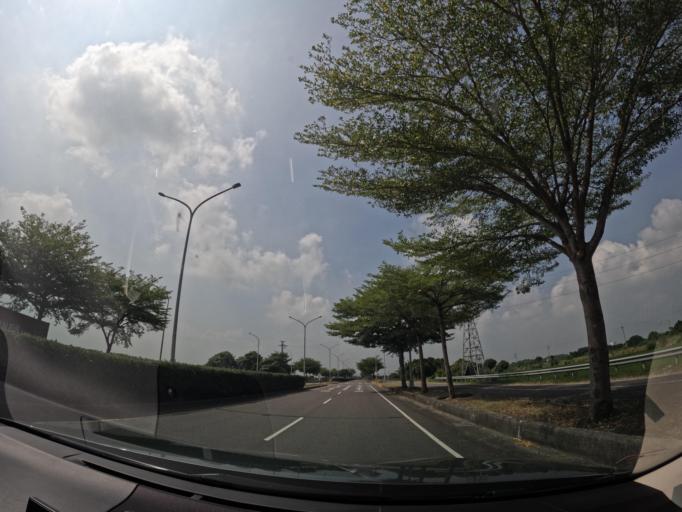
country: TW
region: Taiwan
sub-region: Yunlin
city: Douliu
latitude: 23.7137
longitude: 120.4969
